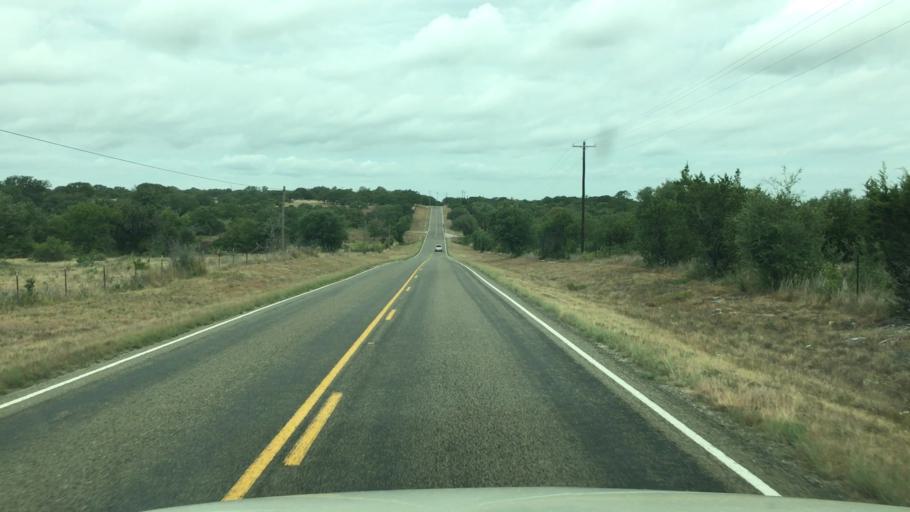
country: US
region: Texas
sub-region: Llano County
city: Horseshoe Bay
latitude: 30.4619
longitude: -98.4040
